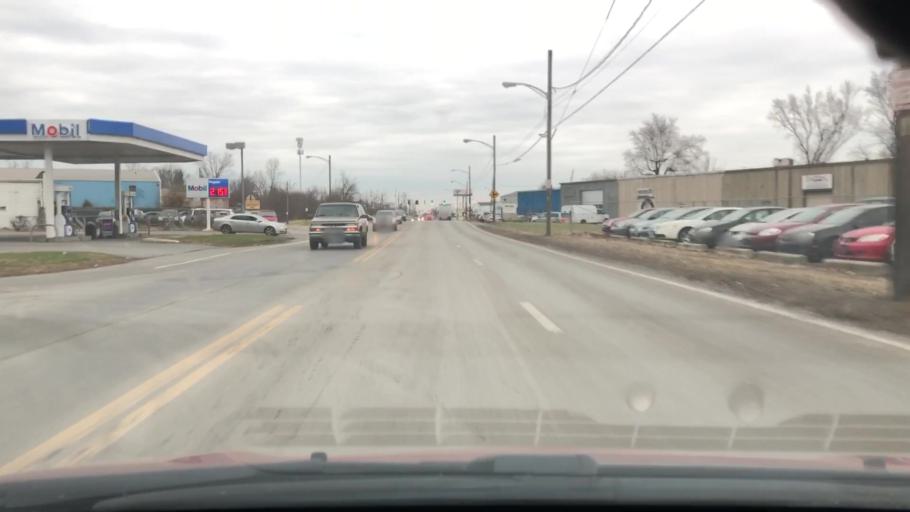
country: US
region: Ohio
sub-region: Franklin County
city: Minerva Park
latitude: 40.0253
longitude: -82.9614
